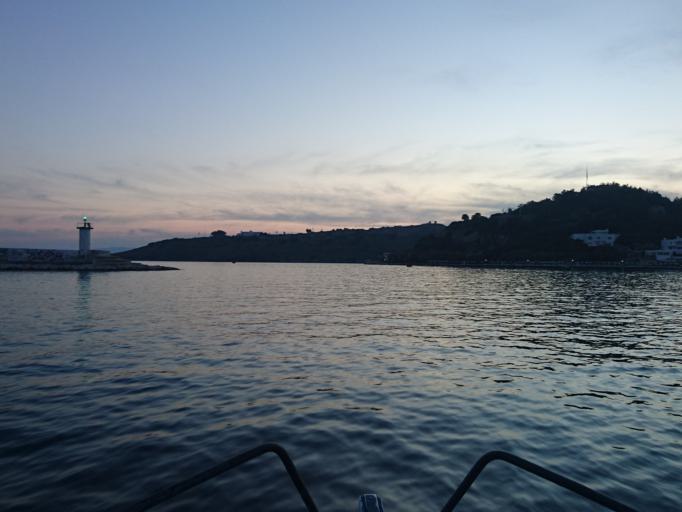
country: TR
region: Mugla
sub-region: Bodrum
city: Bodrum
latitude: 37.0321
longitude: 27.4252
